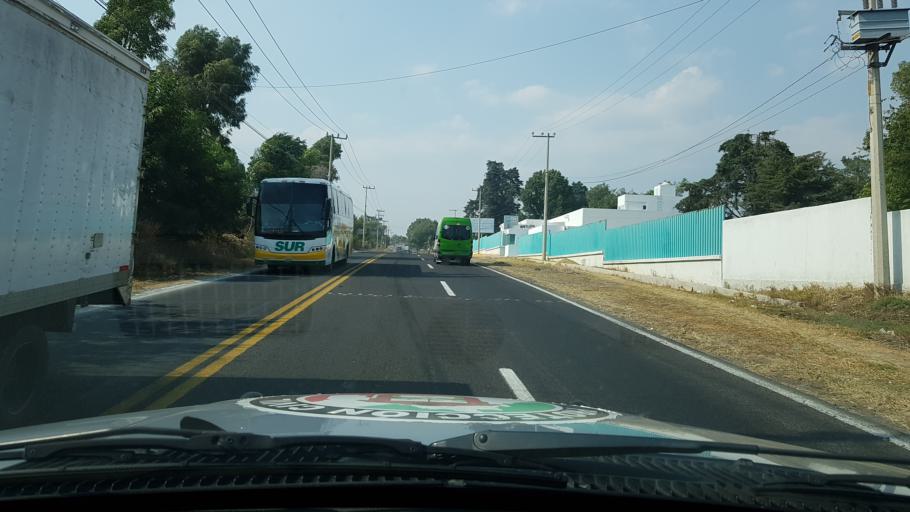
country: MX
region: Mexico
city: Tepetlixpa
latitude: 19.0160
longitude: -98.8244
